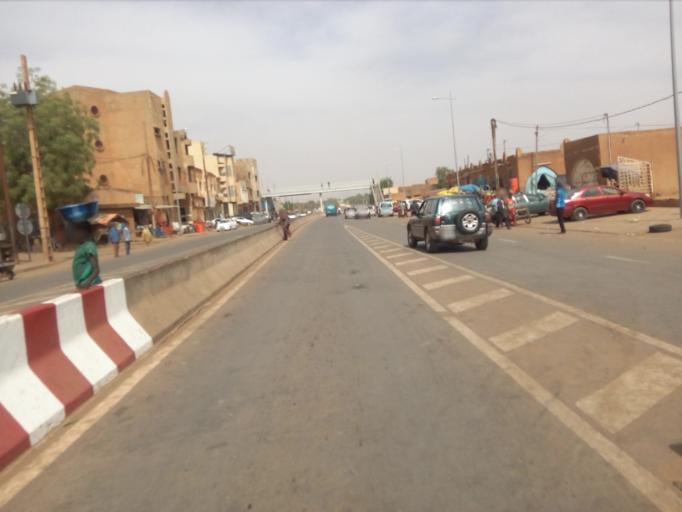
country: NE
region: Niamey
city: Niamey
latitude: 13.5223
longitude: 2.1148
